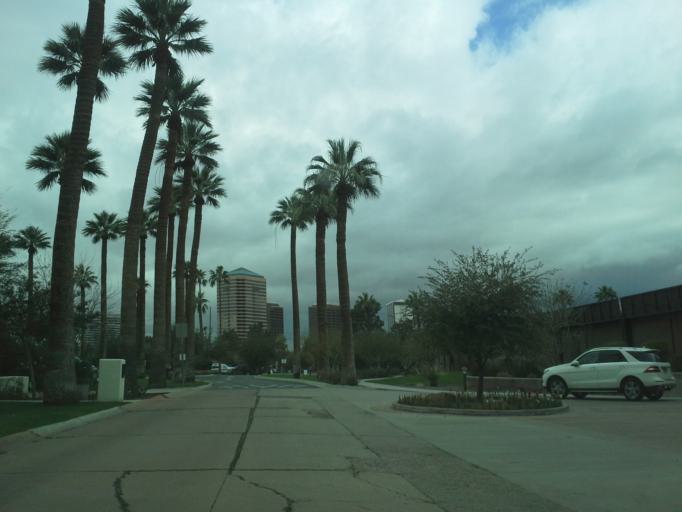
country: US
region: Arizona
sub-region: Maricopa County
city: Phoenix
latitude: 33.4810
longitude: -112.0629
